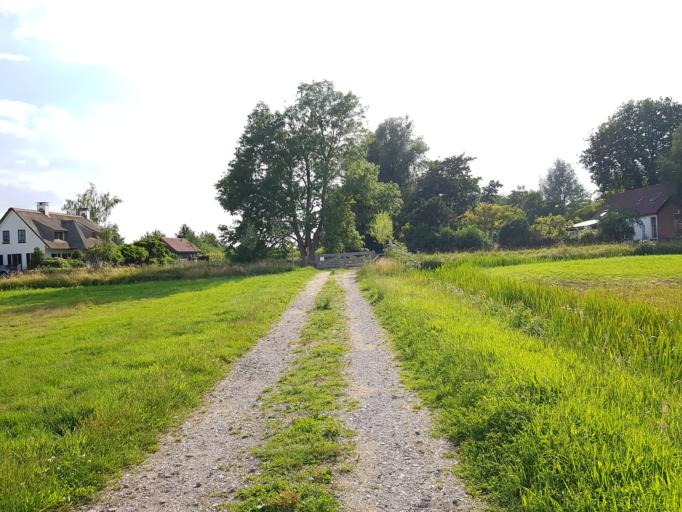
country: NL
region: North Holland
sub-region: Gemeente Wijdemeren
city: Oud-Loosdrecht
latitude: 52.1681
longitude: 5.0939
